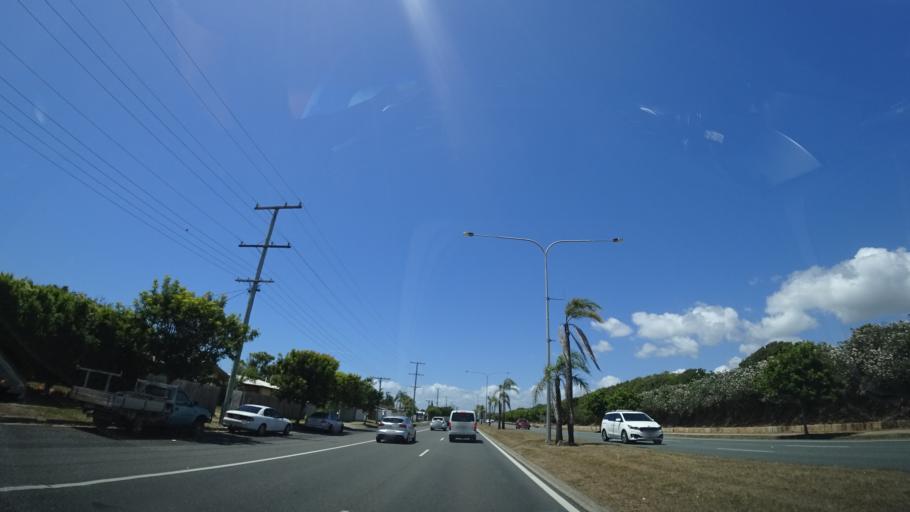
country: AU
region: Queensland
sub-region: Sunshine Coast
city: Mooloolaba
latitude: -26.7159
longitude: 153.1299
